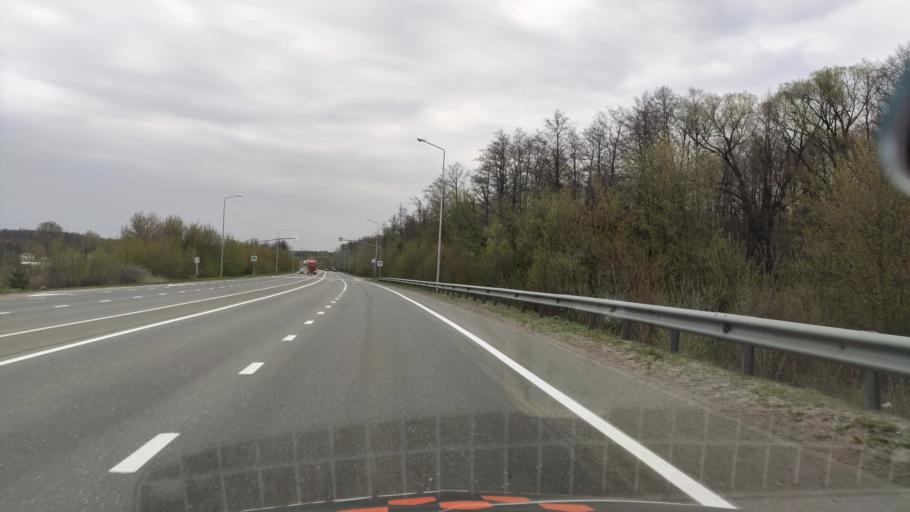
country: RU
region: Belgorod
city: Staryy Oskol
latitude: 51.3481
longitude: 37.8247
